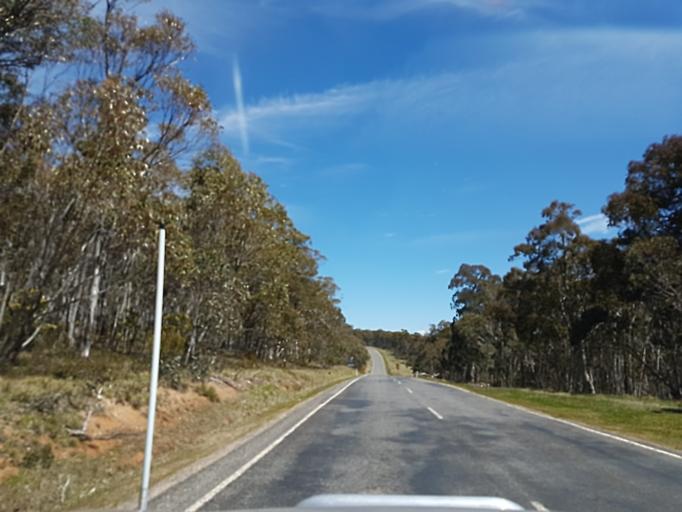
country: AU
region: Victoria
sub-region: Alpine
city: Mount Beauty
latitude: -37.0813
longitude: 147.3723
